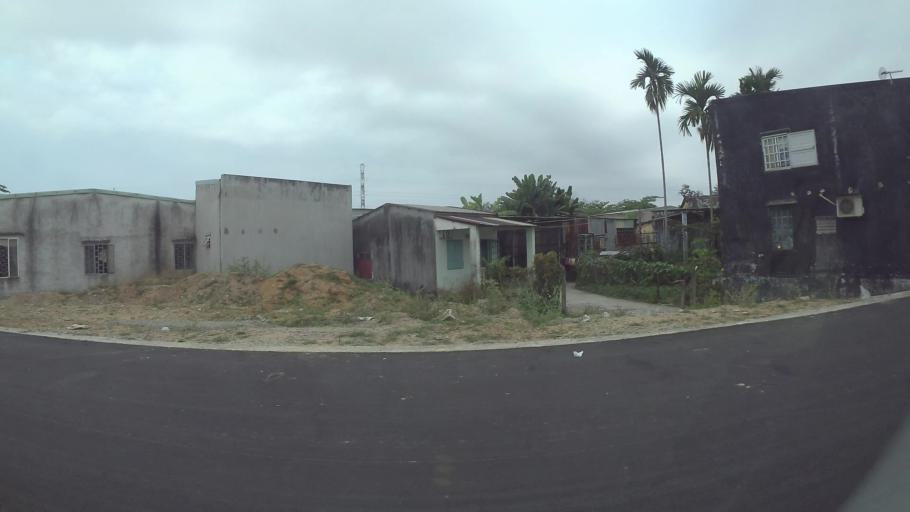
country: VN
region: Da Nang
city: Lien Chieu
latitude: 16.0476
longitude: 108.1679
